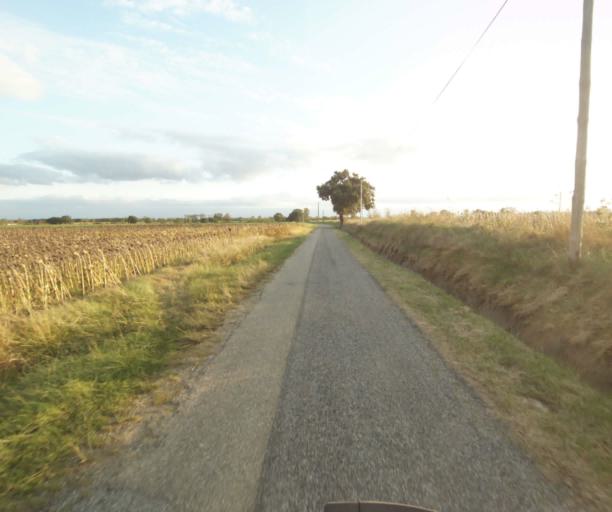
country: FR
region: Midi-Pyrenees
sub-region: Departement de la Haute-Garonne
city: Launac
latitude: 43.8084
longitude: 1.1635
